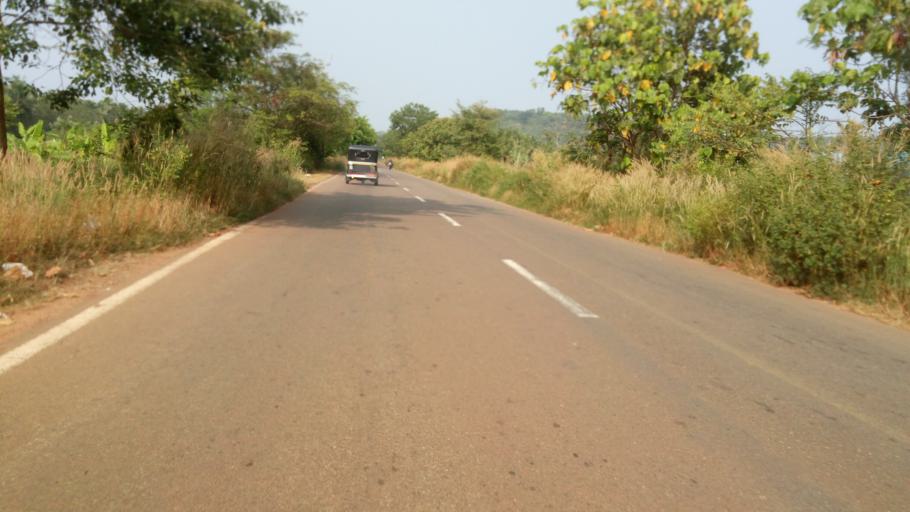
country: IN
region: Kerala
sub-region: Malappuram
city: Malappuram
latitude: 10.9959
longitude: 76.0144
